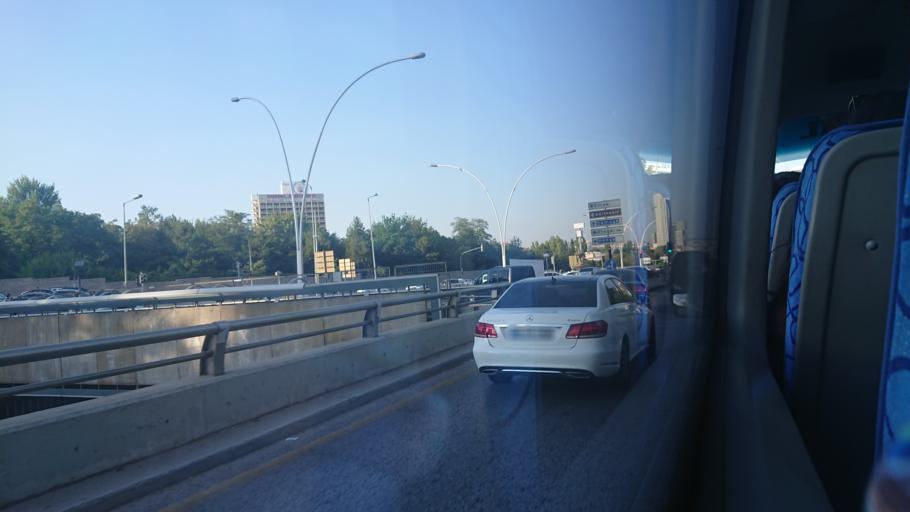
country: TR
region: Ankara
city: Ankara
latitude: 39.9311
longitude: 32.8192
